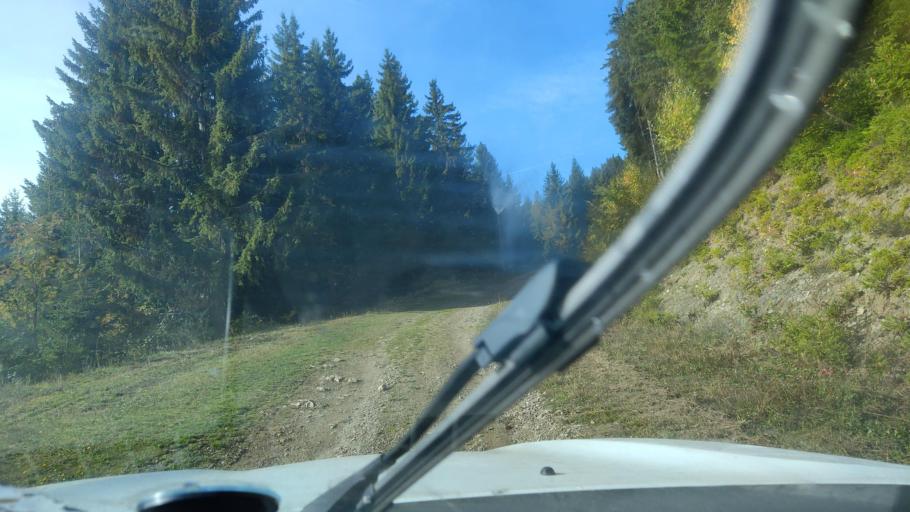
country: FR
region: Rhone-Alpes
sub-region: Departement de la Savoie
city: Beaufort
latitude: 45.7388
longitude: 6.4964
